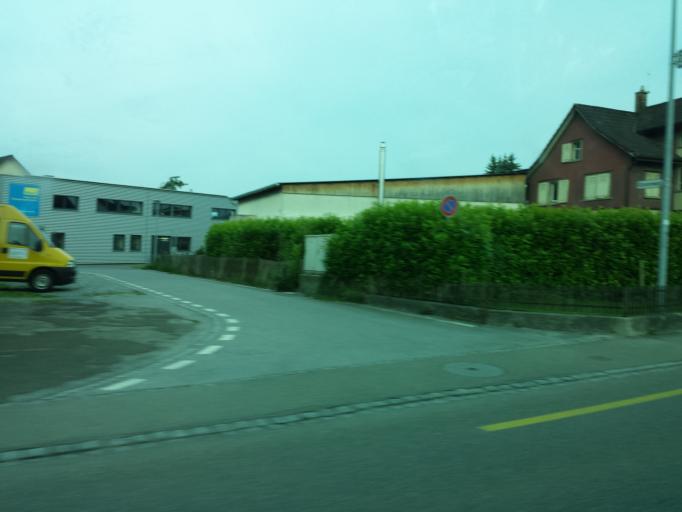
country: CH
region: Saint Gallen
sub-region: Wahlkreis Rheintal
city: Diepoldsau
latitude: 47.3998
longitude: 9.6381
